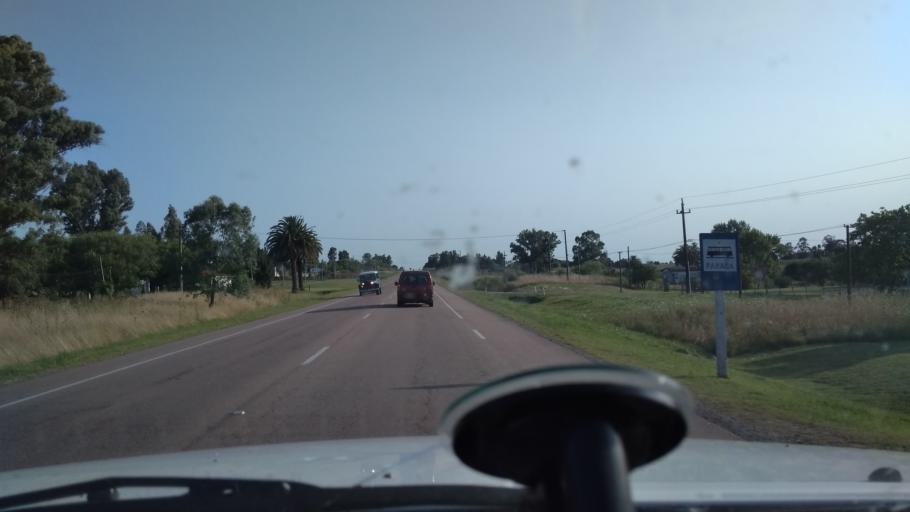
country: UY
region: Canelones
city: Sauce
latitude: -34.6173
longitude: -56.0496
